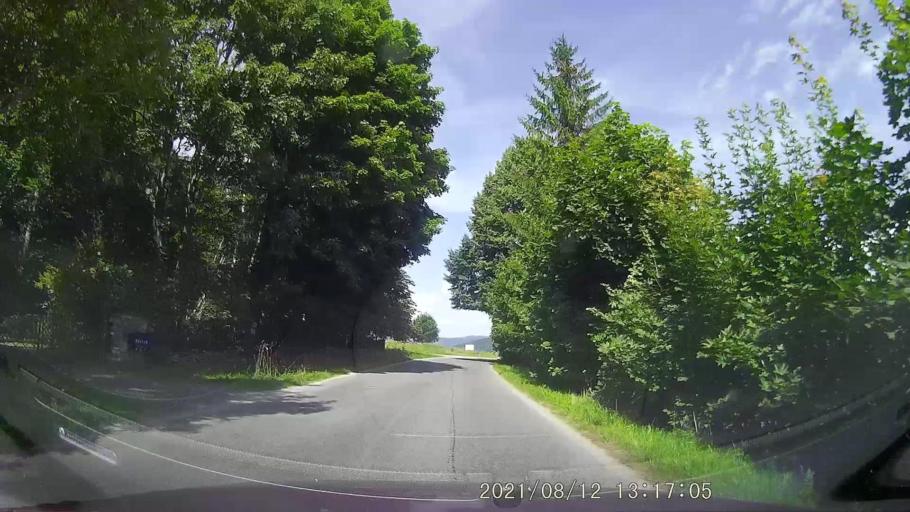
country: PL
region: Lower Silesian Voivodeship
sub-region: Powiat klodzki
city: Stronie Slaskie
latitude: 50.2678
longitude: 16.8809
